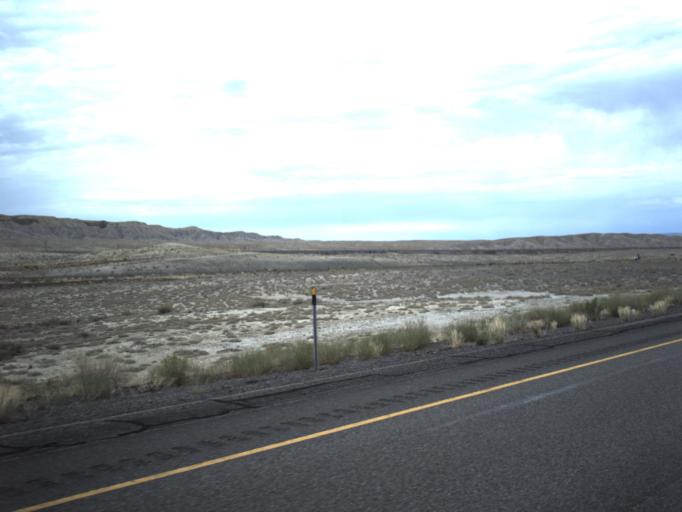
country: US
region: Utah
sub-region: Grand County
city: Moab
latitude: 38.9360
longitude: -109.4751
